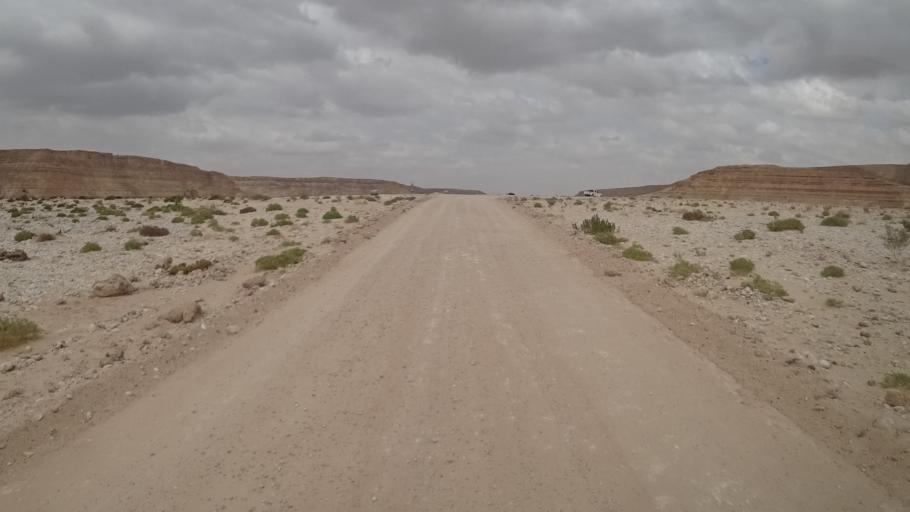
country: YE
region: Al Mahrah
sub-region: Shahan
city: Shihan as Sufla
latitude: 17.4718
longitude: 53.0003
